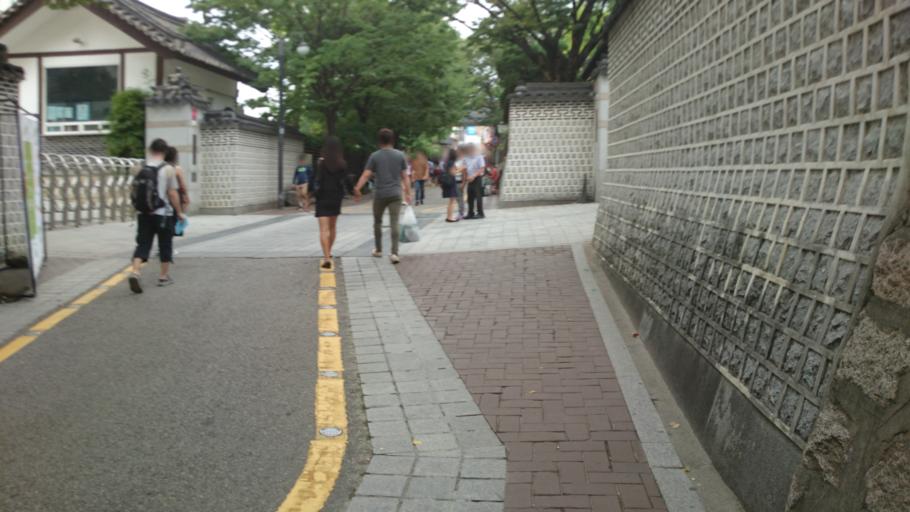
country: KR
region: Seoul
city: Seoul
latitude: 37.5776
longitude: 126.9824
